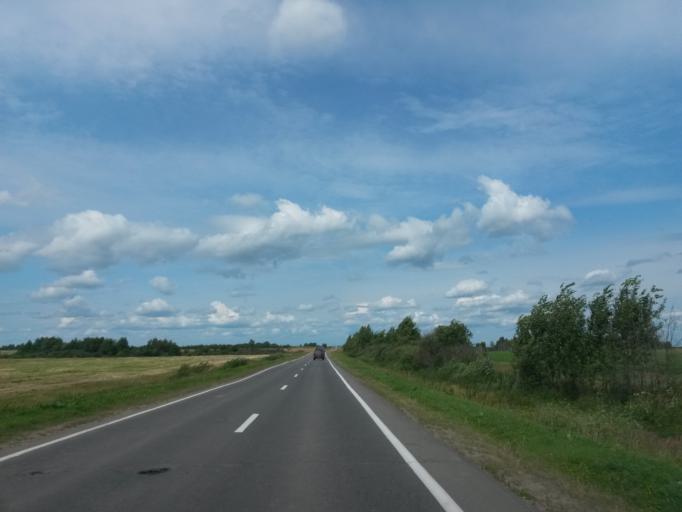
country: RU
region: Jaroslavl
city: Yaroslavl
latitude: 57.7444
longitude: 39.8857
